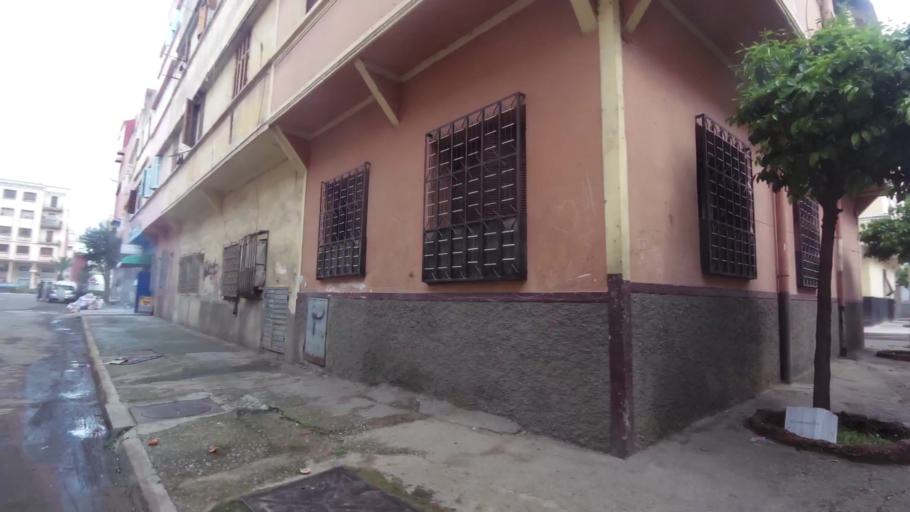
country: MA
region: Chaouia-Ouardigha
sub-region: Settat Province
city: Berrechid
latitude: 33.2731
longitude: -7.5869
